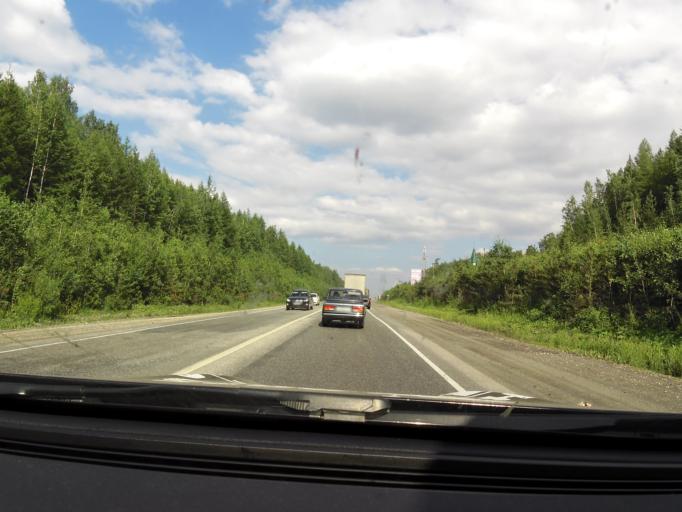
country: RU
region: Sverdlovsk
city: Talitsa
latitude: 56.8489
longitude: 60.0477
